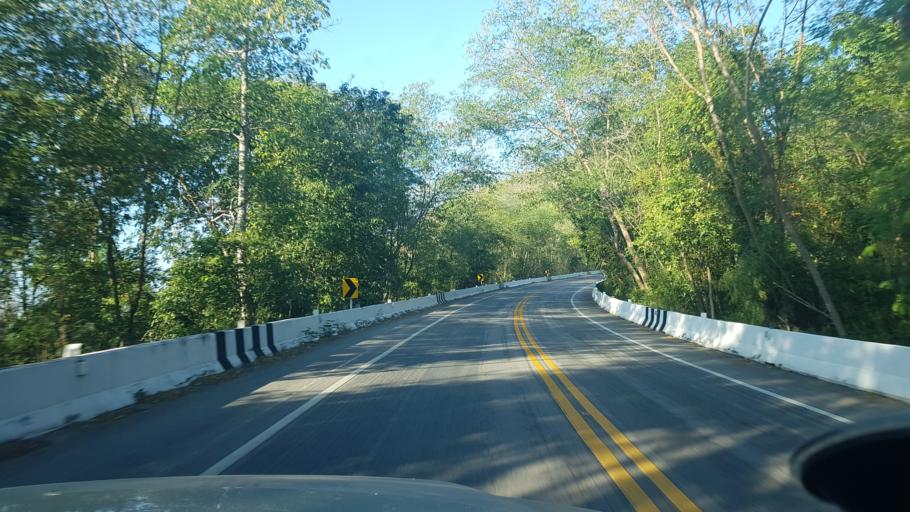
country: TH
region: Khon Kaen
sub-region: Amphoe Phu Pha Man
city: Phu Pha Man
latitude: 16.6459
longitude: 101.7919
